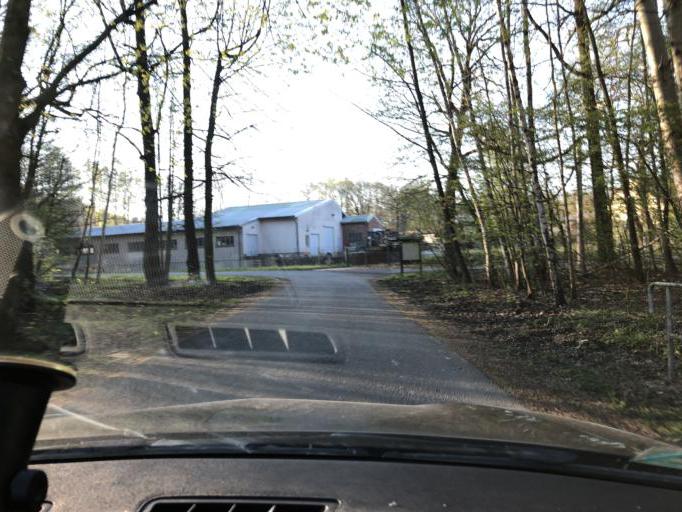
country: DE
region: Saxony
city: Krauschwitz
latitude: 51.5126
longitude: 14.7160
